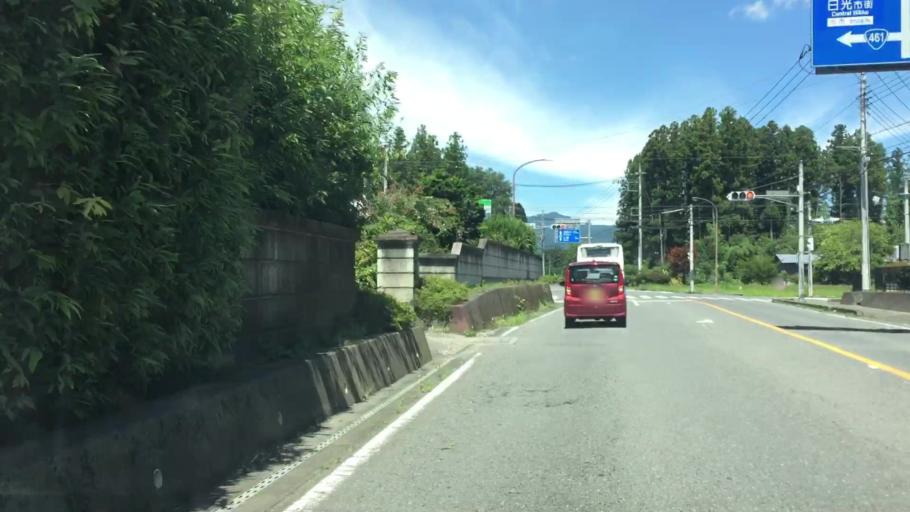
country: JP
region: Tochigi
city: Imaichi
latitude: 36.7489
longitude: 139.7356
